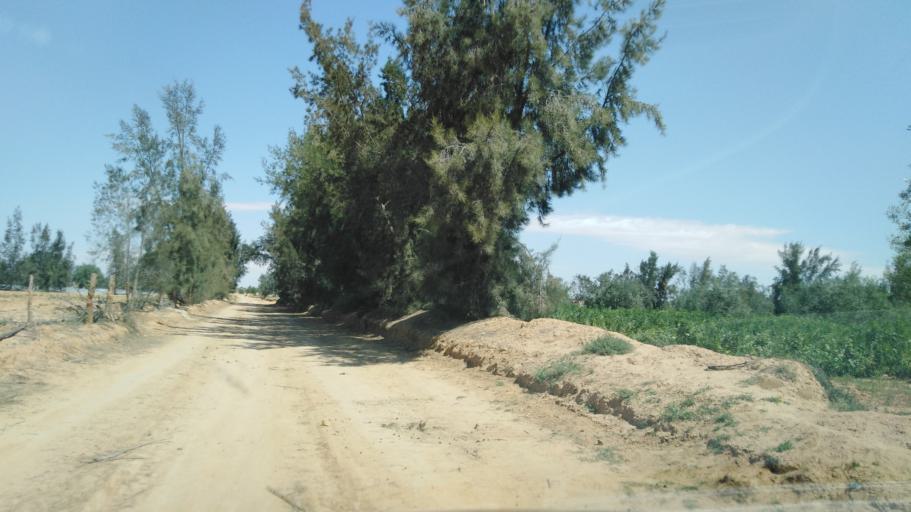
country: TN
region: Safaqis
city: Sfax
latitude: 34.7658
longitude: 10.5281
